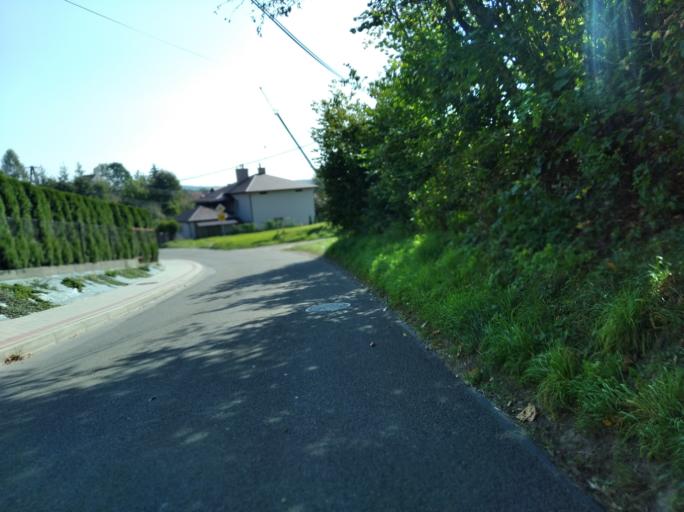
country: PL
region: Subcarpathian Voivodeship
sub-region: Powiat strzyzowski
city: Czudec
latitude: 49.9476
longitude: 21.8382
